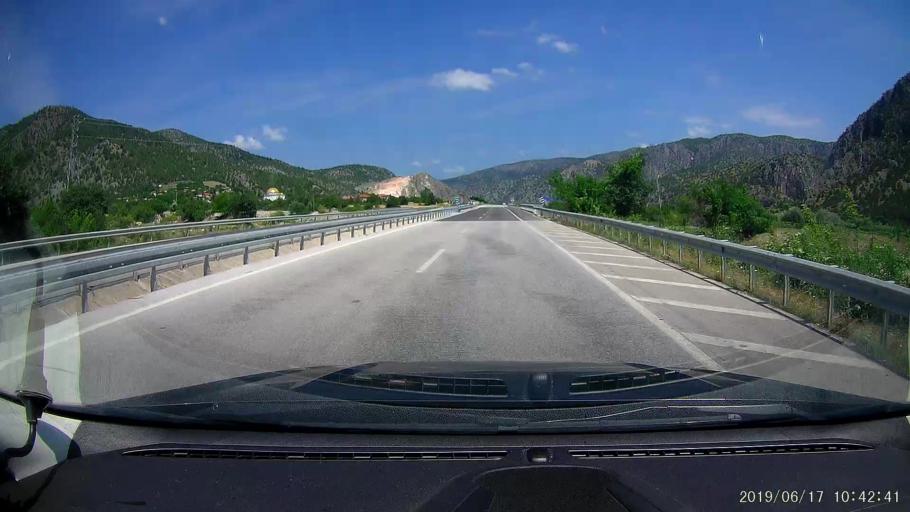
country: TR
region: Corum
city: Hacihamza
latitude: 41.0506
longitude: 34.5486
